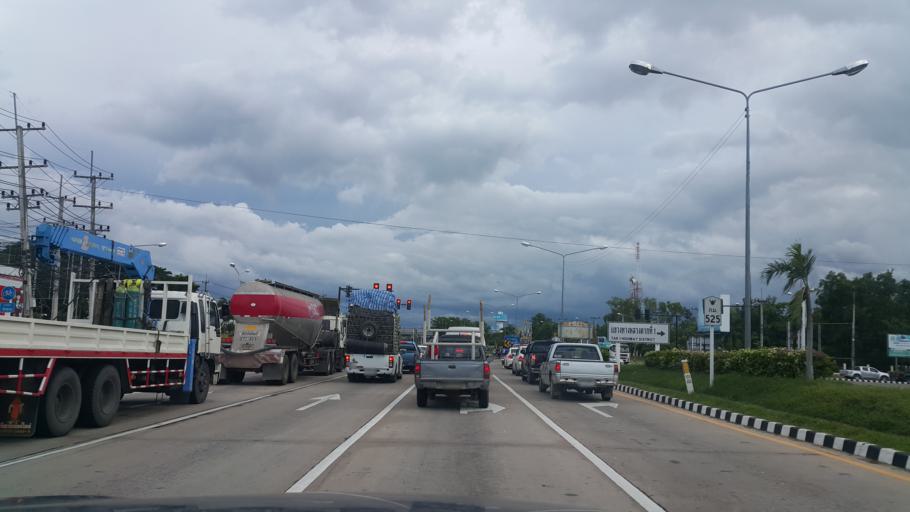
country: TH
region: Tak
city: Tak
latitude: 16.8859
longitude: 99.1275
